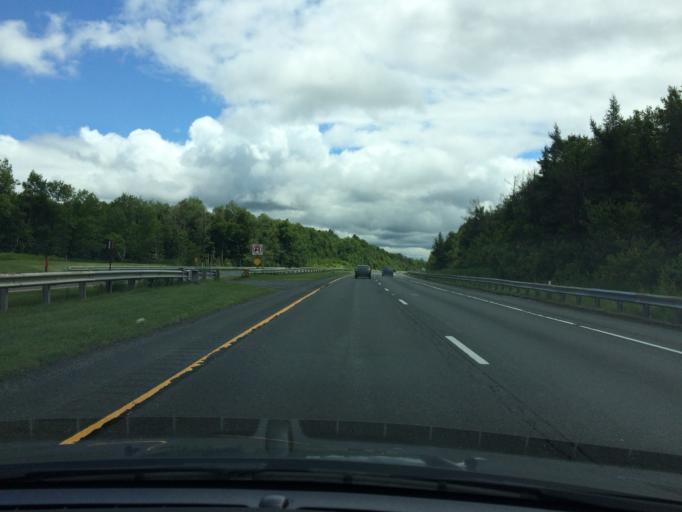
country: US
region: Massachusetts
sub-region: Berkshire County
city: Otis
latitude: 42.2447
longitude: -73.0782
